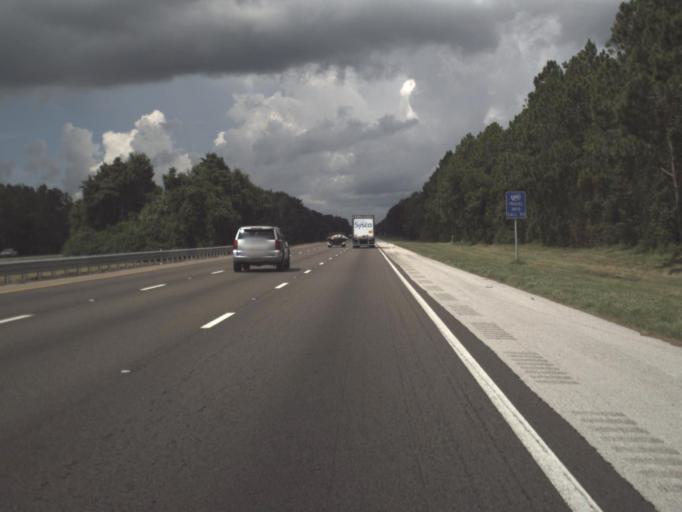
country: US
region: Florida
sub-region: Hillsborough County
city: Ruskin
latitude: 27.6502
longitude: -82.4454
